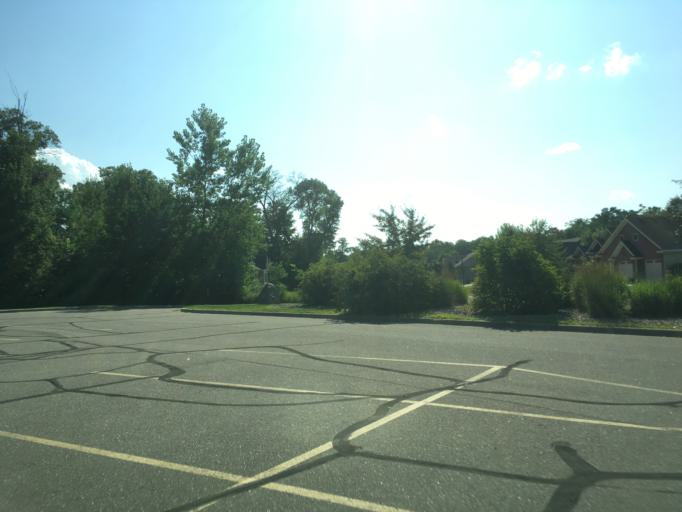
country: US
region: Minnesota
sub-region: Stearns County
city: Sartell
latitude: 45.6626
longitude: -94.2448
